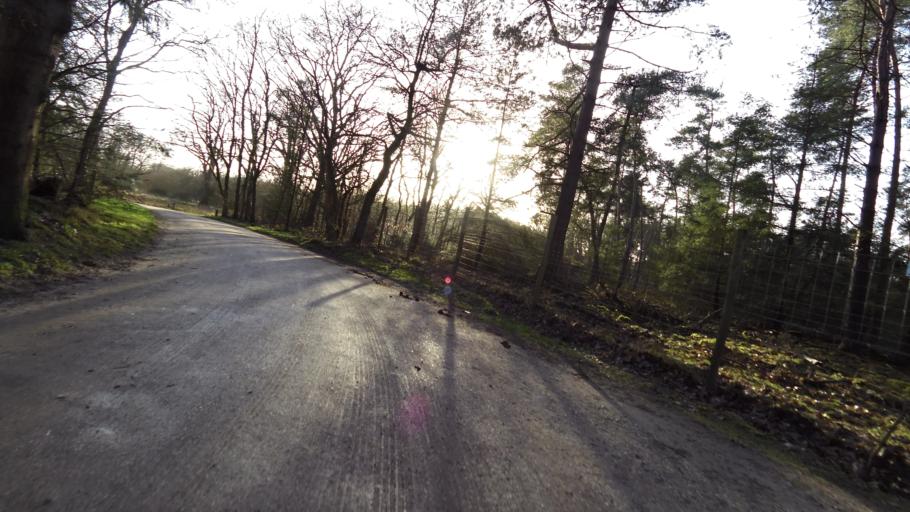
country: NL
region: Gelderland
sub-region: Gemeente Epe
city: Vaassen
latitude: 52.2577
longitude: 5.9186
